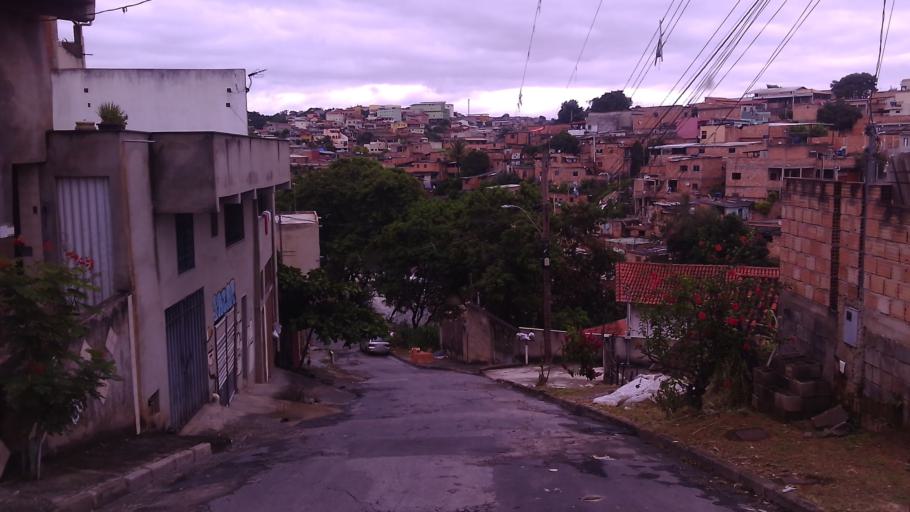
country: BR
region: Minas Gerais
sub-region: Santa Luzia
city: Santa Luzia
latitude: -19.8392
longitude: -43.9050
